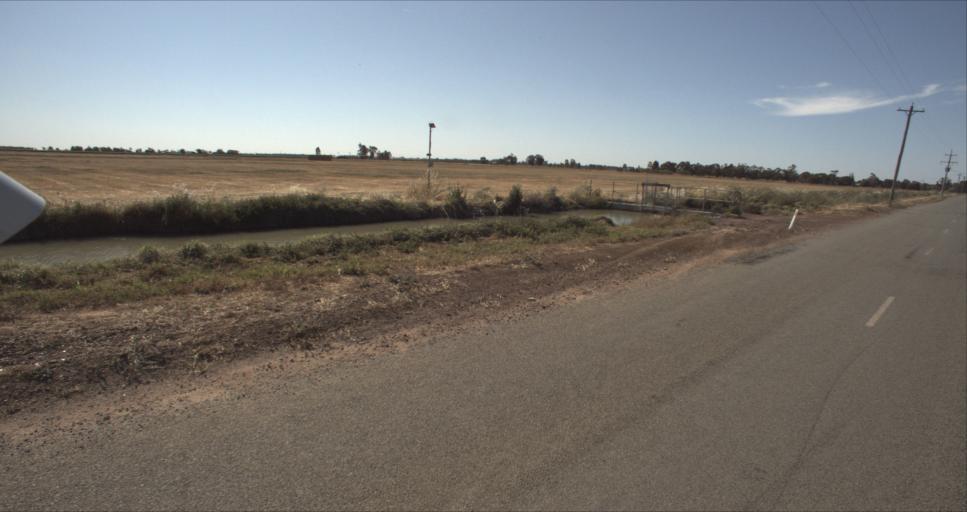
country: AU
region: New South Wales
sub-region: Leeton
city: Leeton
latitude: -34.5755
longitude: 146.3809
